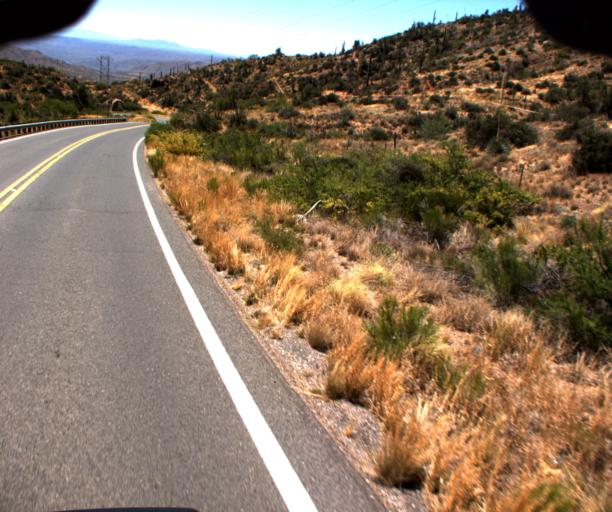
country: US
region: Arizona
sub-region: Pinal County
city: Superior
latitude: 33.2023
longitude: -111.0566
